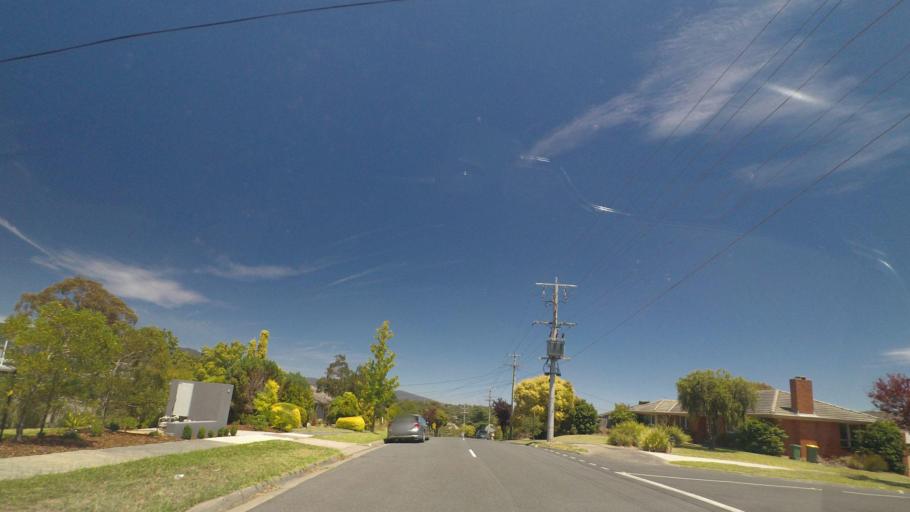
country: AU
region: Victoria
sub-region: Maroondah
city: Croydon North
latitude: -37.7819
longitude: 145.3168
